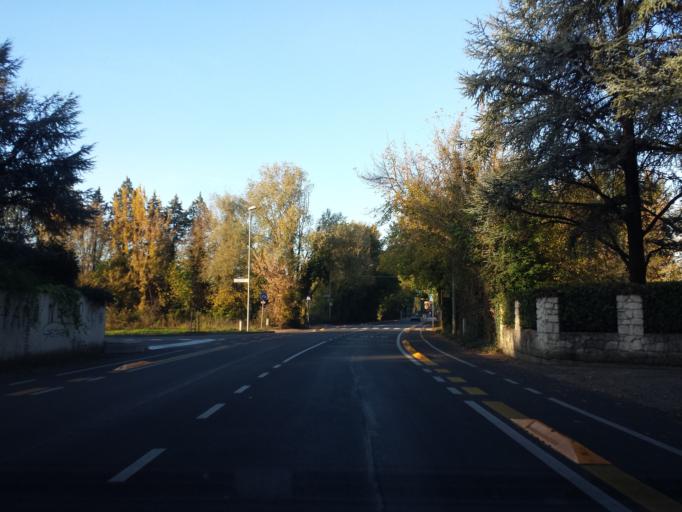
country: IT
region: Veneto
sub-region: Provincia di Vicenza
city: Vicenza
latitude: 45.5691
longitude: 11.5431
